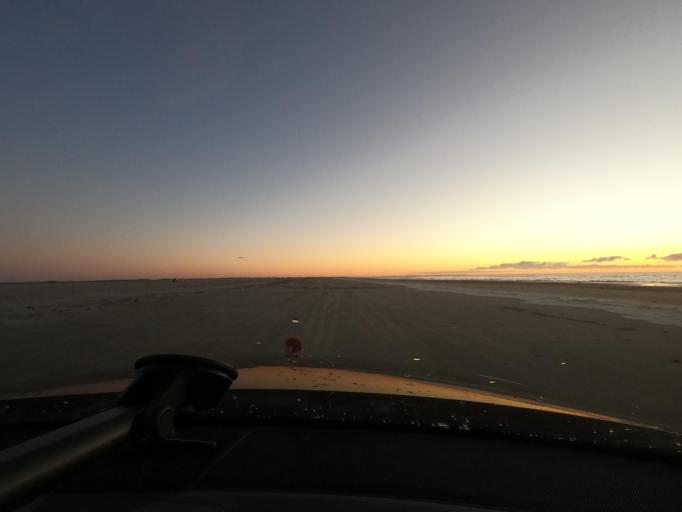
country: DE
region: Schleswig-Holstein
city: List
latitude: 55.1579
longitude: 8.4772
